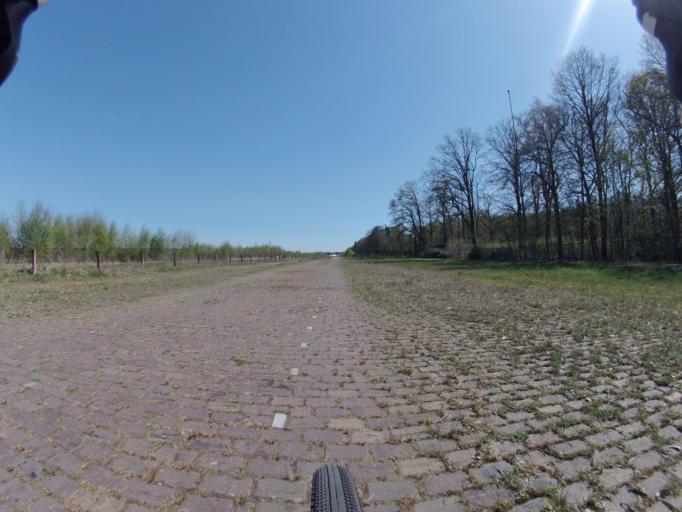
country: NL
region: Overijssel
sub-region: Gemeente Enschede
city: Enschede
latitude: 52.2675
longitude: 6.8820
